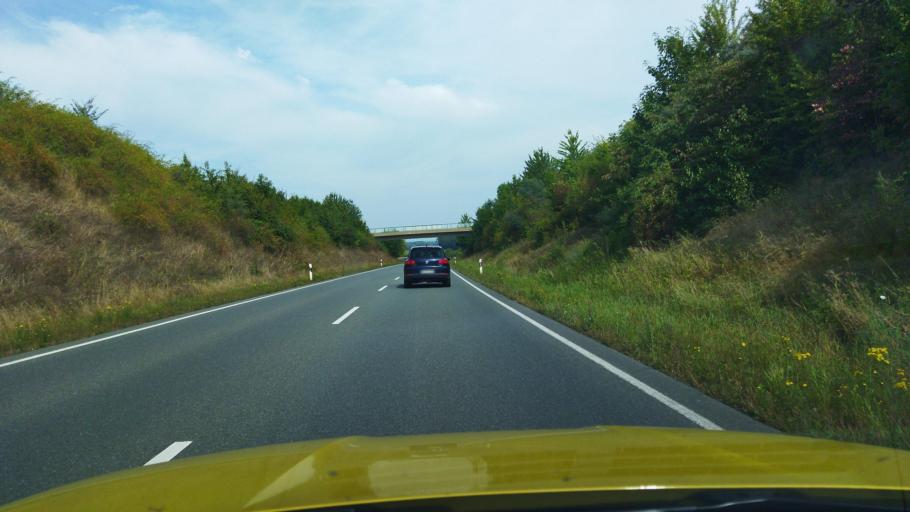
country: DE
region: North Rhine-Westphalia
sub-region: Regierungsbezirk Munster
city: Ennigerloh
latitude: 51.8643
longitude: 8.0271
